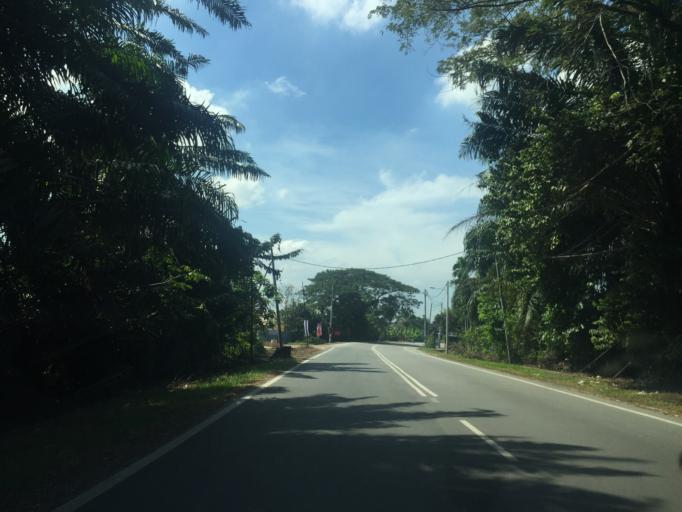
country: MY
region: Penang
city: Tasek Glugor
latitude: 5.5055
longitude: 100.5272
